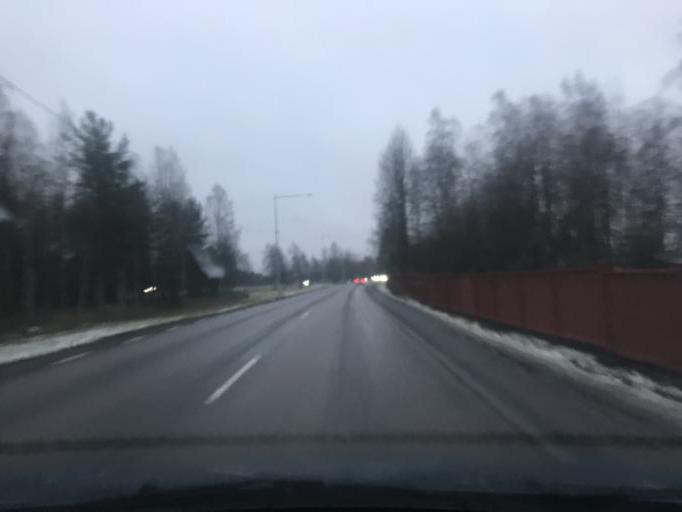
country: SE
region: Norrbotten
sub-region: Lulea Kommun
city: Gammelstad
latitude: 65.6532
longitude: 21.9815
